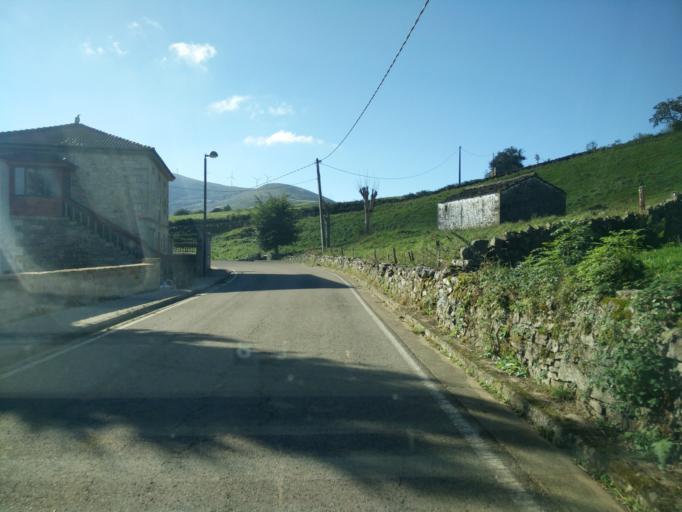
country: ES
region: Cantabria
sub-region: Provincia de Cantabria
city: San Pedro del Romeral
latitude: 43.1110
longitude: -3.8186
